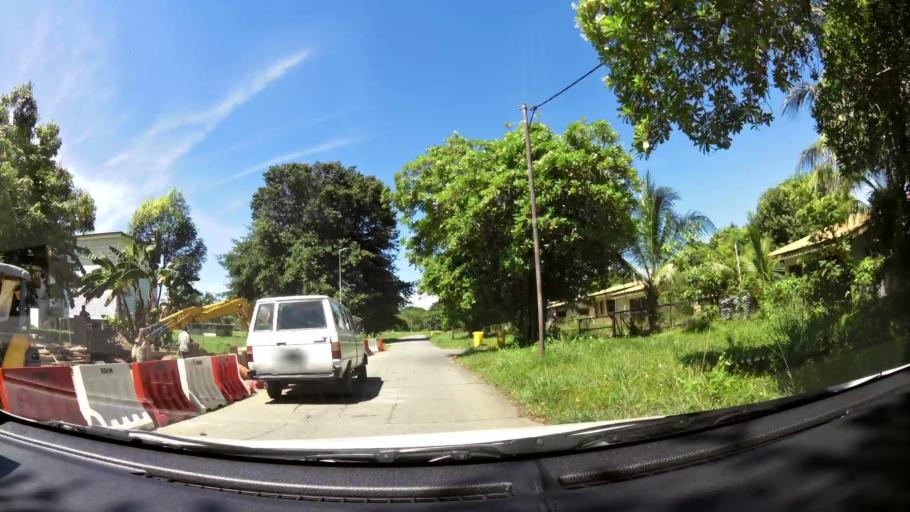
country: BN
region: Brunei and Muara
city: Bandar Seri Begawan
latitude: 5.0337
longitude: 115.0681
